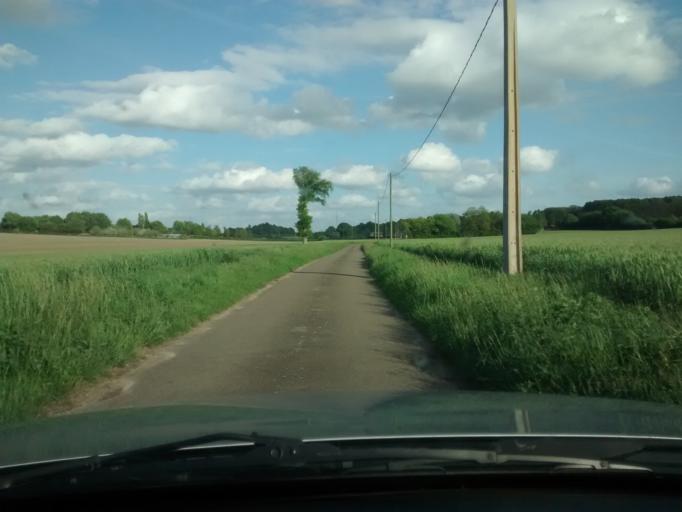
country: FR
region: Pays de la Loire
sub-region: Departement de la Sarthe
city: Challes
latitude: 47.9576
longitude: 0.4486
